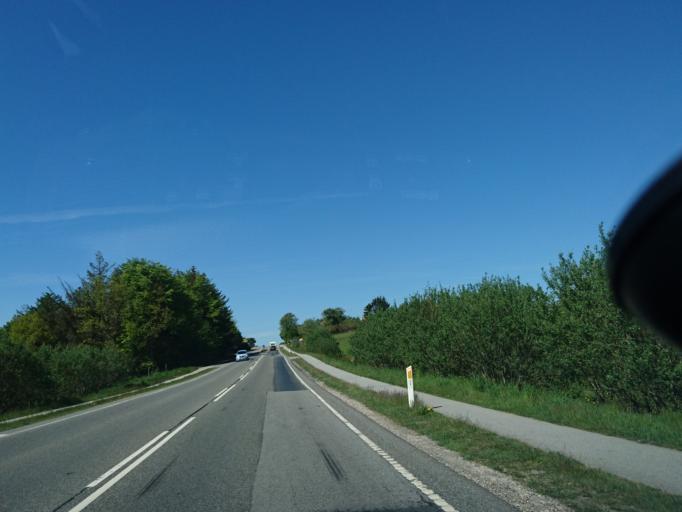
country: DK
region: North Denmark
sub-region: Hjorring Kommune
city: Tars
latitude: 57.4554
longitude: 10.1312
